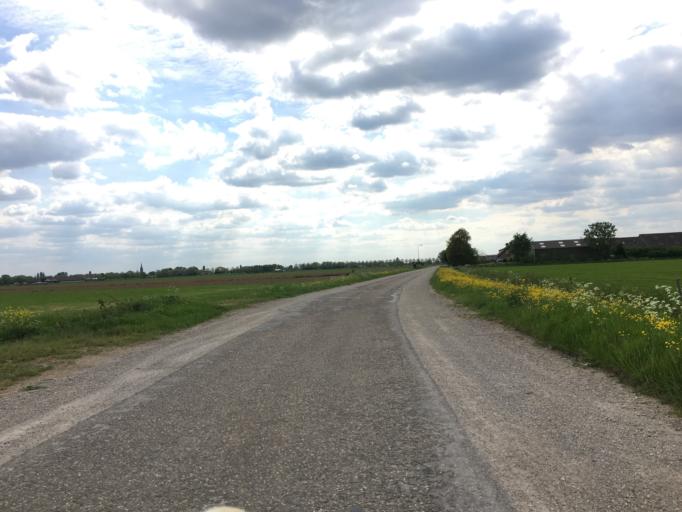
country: NL
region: Gelderland
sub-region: Gemeente Maasdriel
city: Hedel
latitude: 51.7180
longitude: 5.2399
